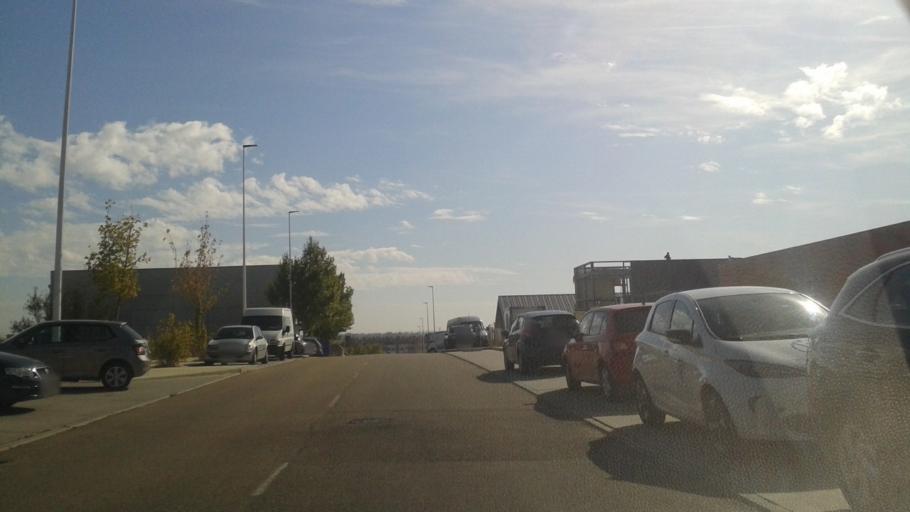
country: ES
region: Castille and Leon
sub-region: Provincia de Valladolid
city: Arroyo
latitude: 41.6277
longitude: -4.7684
